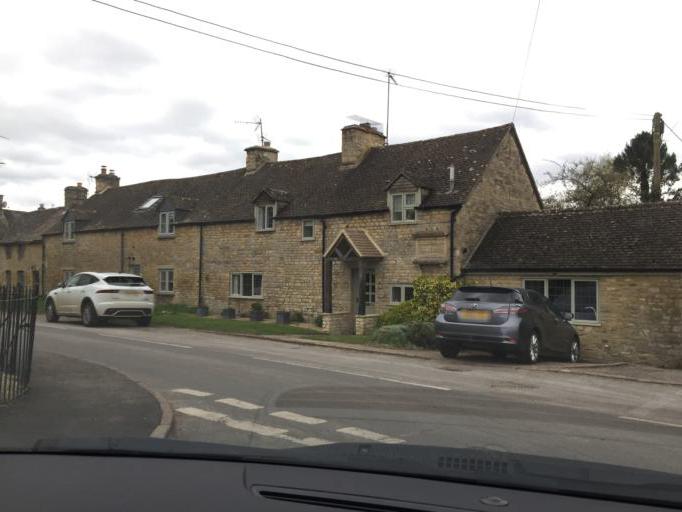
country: GB
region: England
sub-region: Oxfordshire
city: Chipping Norton
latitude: 51.9525
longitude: -1.5418
